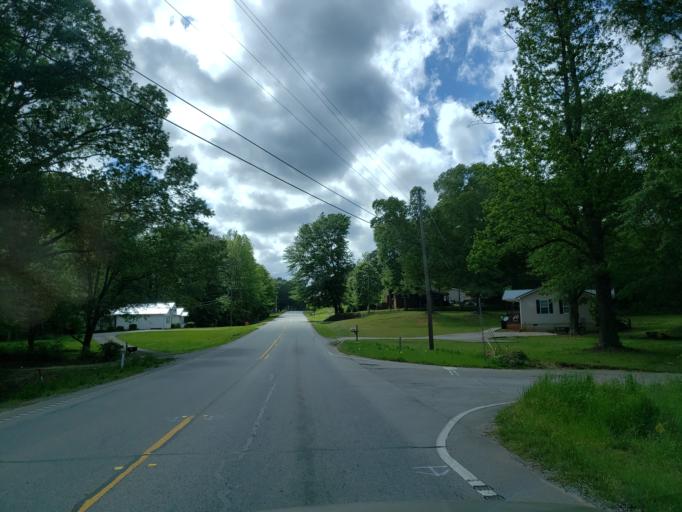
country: US
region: Georgia
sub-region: Haralson County
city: Bremen
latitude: 33.7049
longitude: -85.1889
